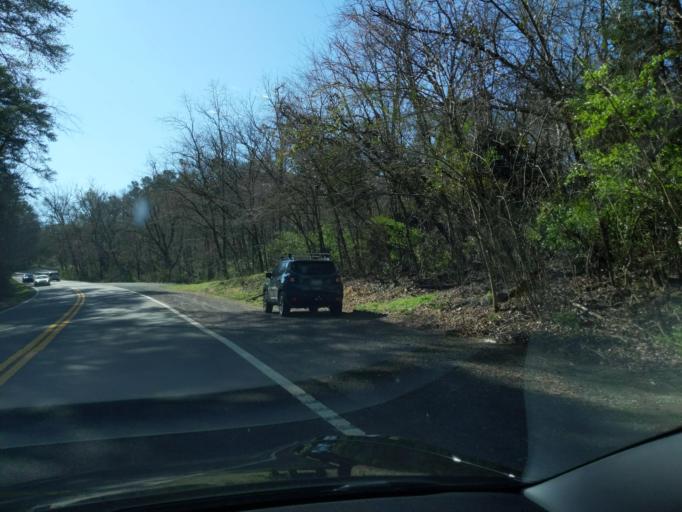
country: US
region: Tennessee
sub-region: Sevier County
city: Sevierville
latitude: 35.9566
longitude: -83.5459
